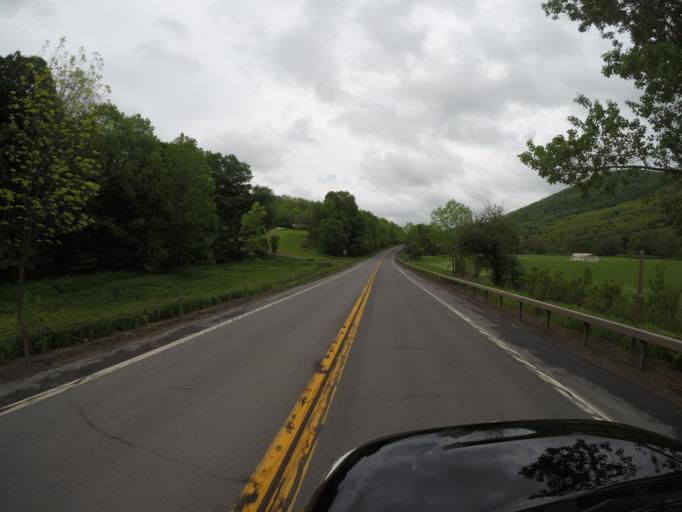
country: US
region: New York
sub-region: Delaware County
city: Delhi
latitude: 42.2561
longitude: -74.8585
